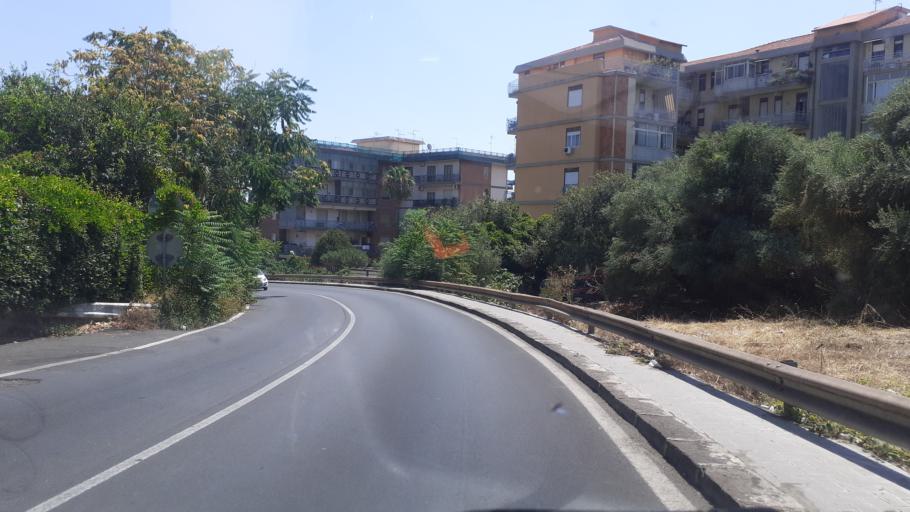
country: IT
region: Sicily
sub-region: Catania
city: Canalicchio
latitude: 37.5381
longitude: 15.0965
